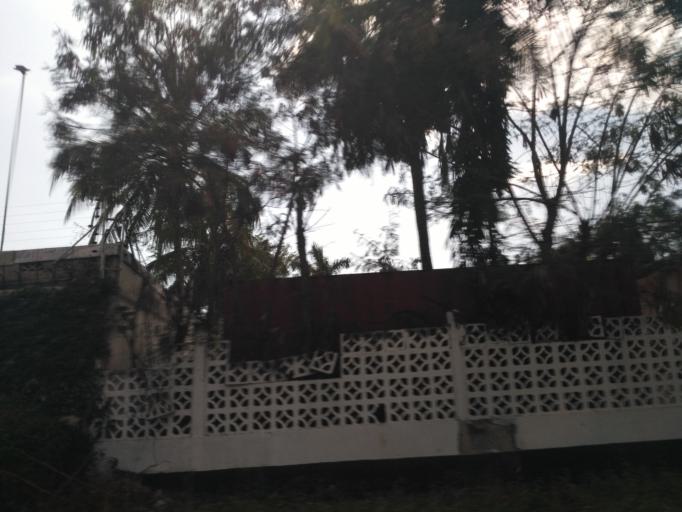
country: TZ
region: Dar es Salaam
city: Magomeni
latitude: -6.7573
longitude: 39.2792
